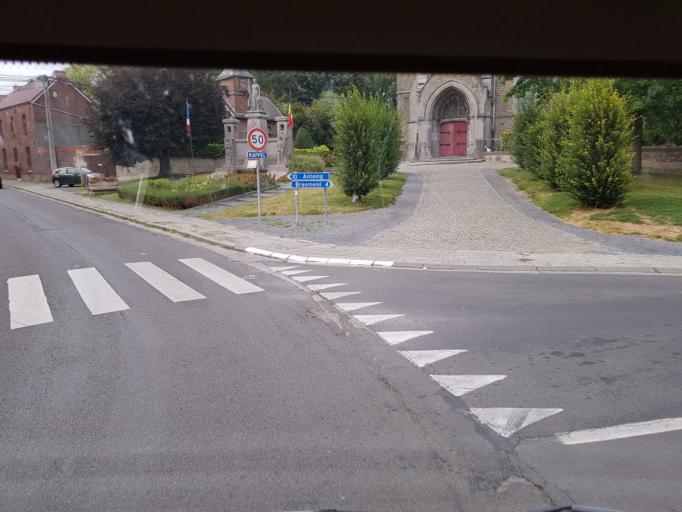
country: FR
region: Nord-Pas-de-Calais
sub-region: Departement du Nord
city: Hergnies
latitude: 50.5084
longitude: 3.5327
